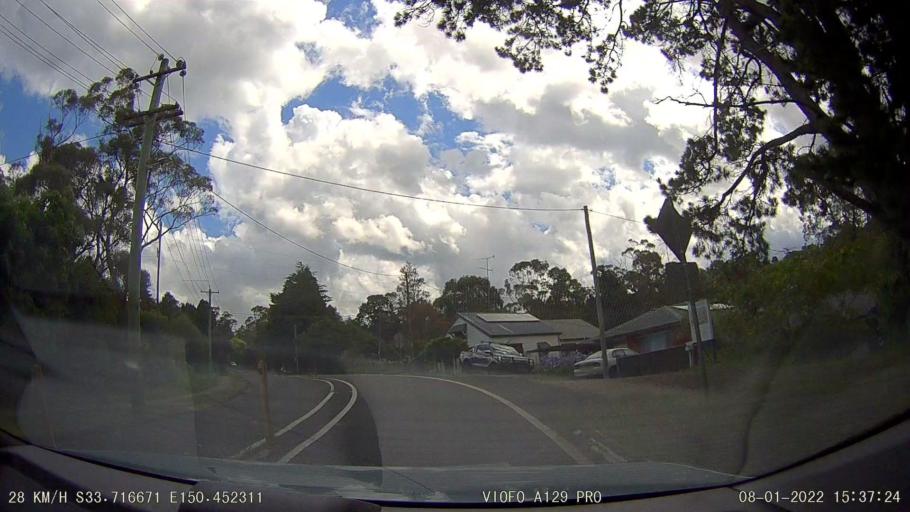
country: AU
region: New South Wales
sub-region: Blue Mountains Municipality
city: Hazelbrook
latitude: -33.7166
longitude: 150.4523
